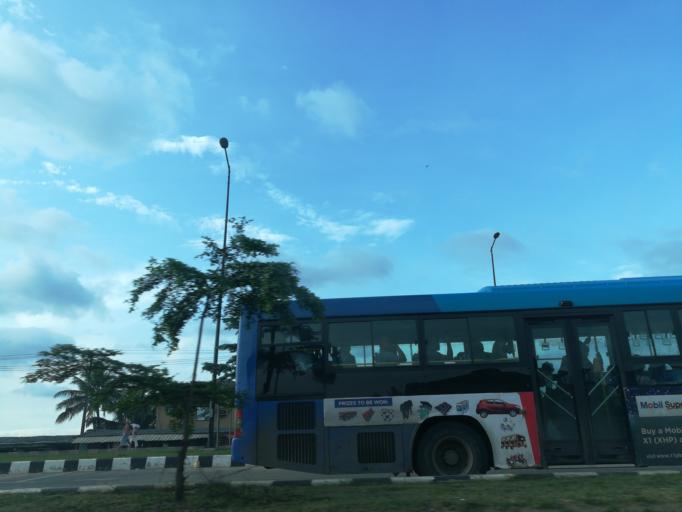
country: NG
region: Lagos
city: Ebute Ikorodu
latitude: 6.6194
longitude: 3.4714
